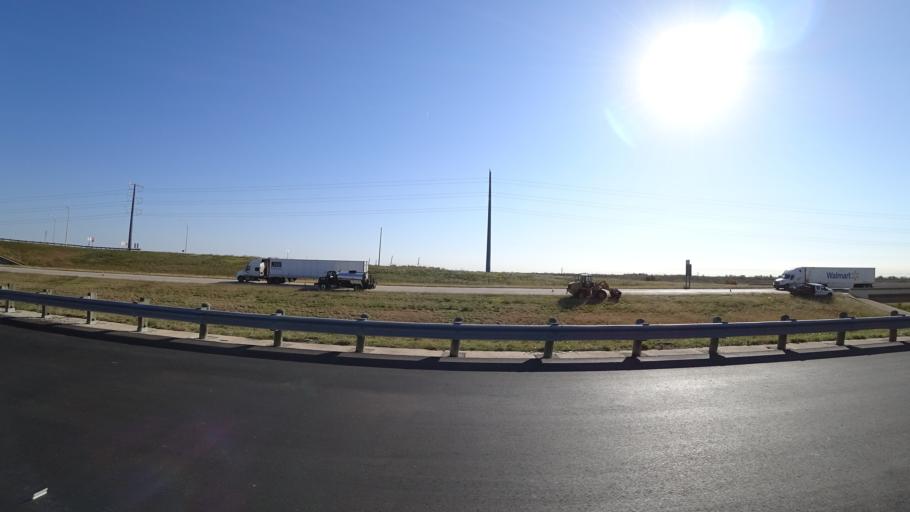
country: US
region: Texas
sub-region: Travis County
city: Onion Creek
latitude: 30.1165
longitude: -97.6608
